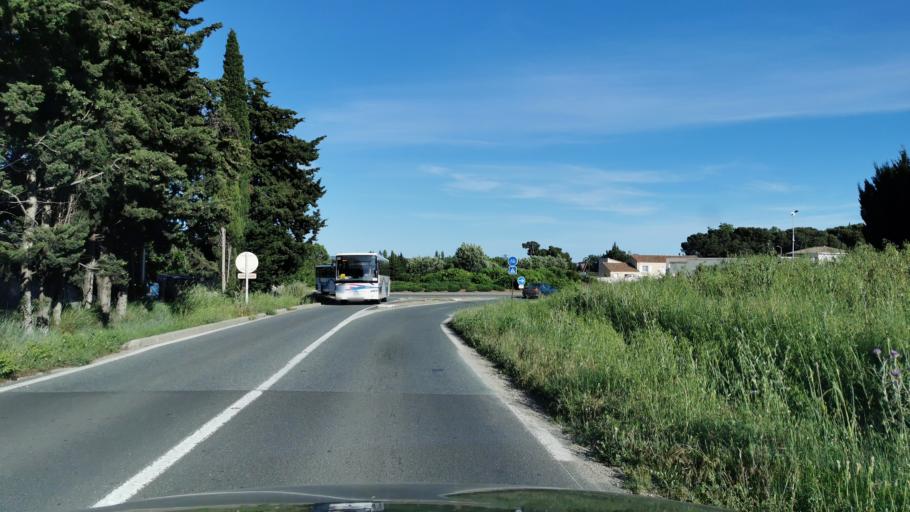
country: FR
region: Languedoc-Roussillon
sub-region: Departement de l'Aude
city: Narbonne
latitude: 43.1987
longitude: 2.9724
